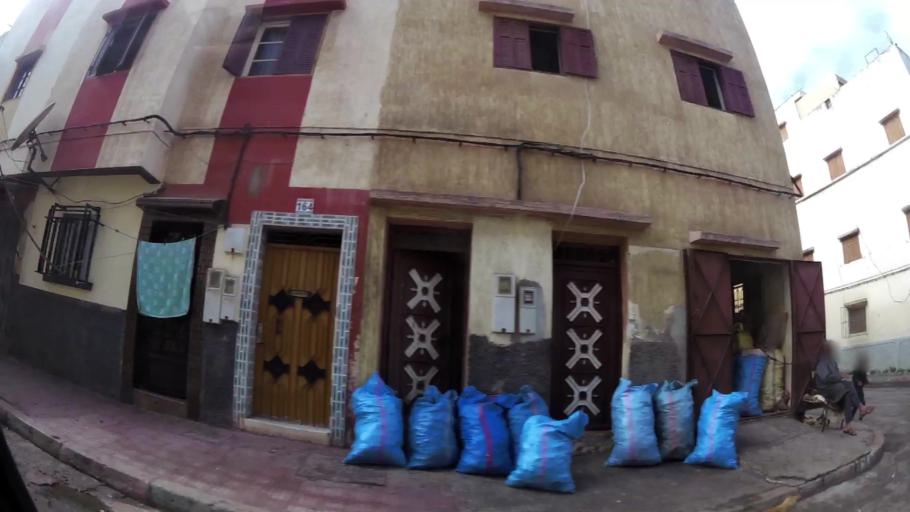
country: MA
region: Grand Casablanca
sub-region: Mohammedia
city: Mohammedia
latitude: 33.6751
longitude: -7.3873
